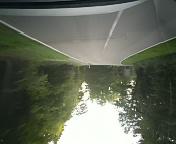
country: DE
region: Baden-Wuerttemberg
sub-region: Karlsruhe Region
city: Neuenburg
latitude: 48.8352
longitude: 8.5562
